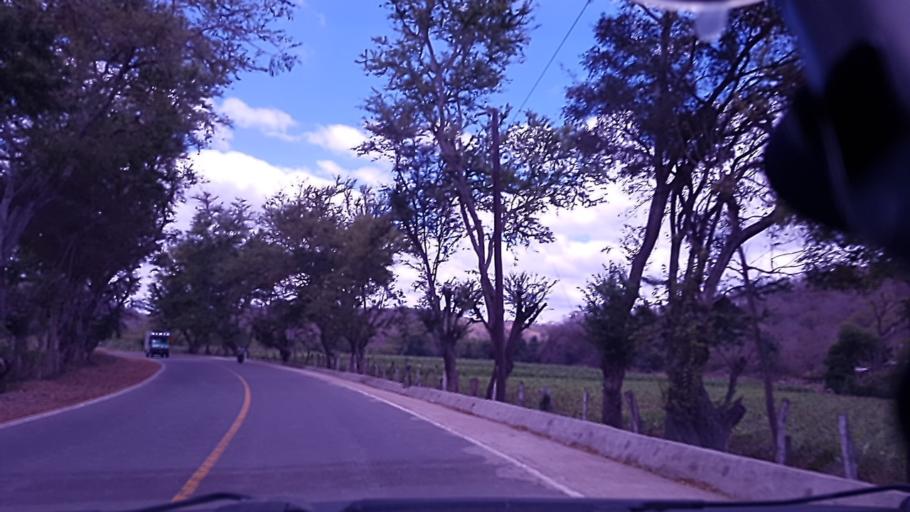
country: NI
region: Esteli
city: Condega
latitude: 13.3740
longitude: -86.3847
